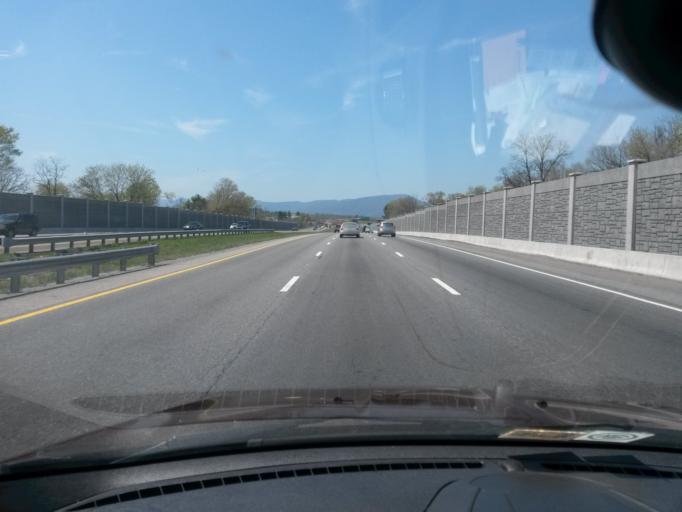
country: US
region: Virginia
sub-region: City of Roanoke
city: Roanoke
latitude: 37.2943
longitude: -79.9492
